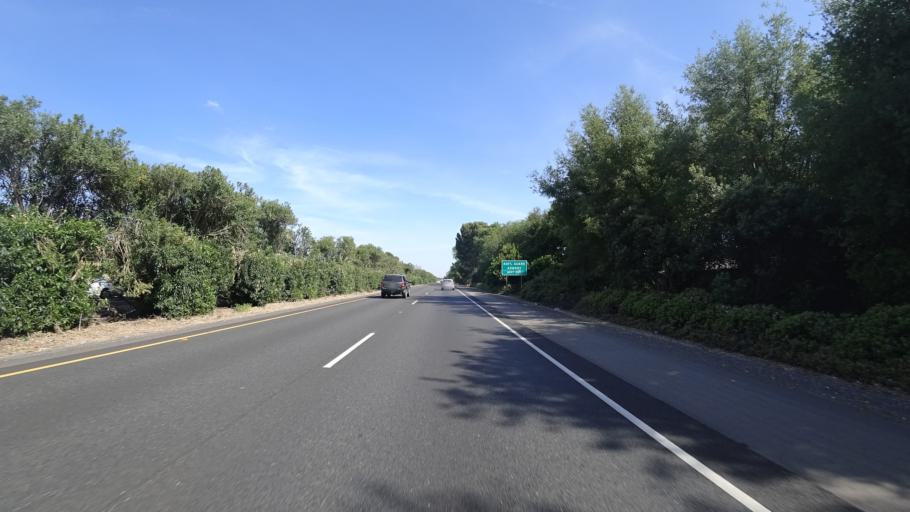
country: US
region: California
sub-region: Butte County
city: Chico
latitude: 39.7694
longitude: -121.8672
